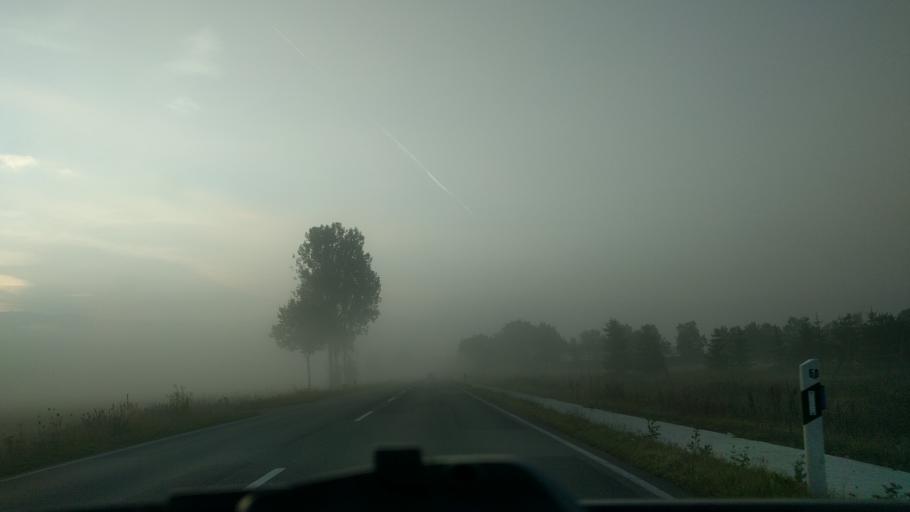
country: DE
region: Lower Saxony
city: Isenbuttel
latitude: 52.4538
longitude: 10.5818
